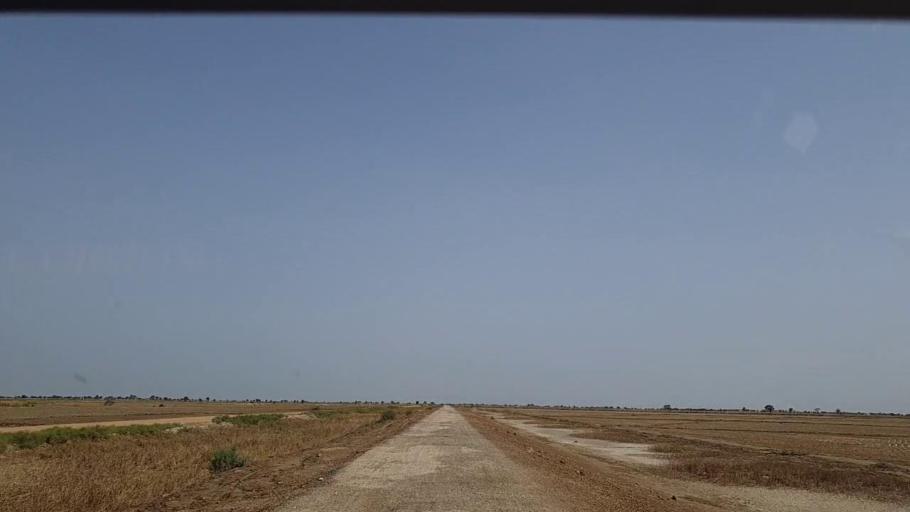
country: PK
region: Sindh
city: Johi
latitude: 26.7881
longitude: 67.6445
